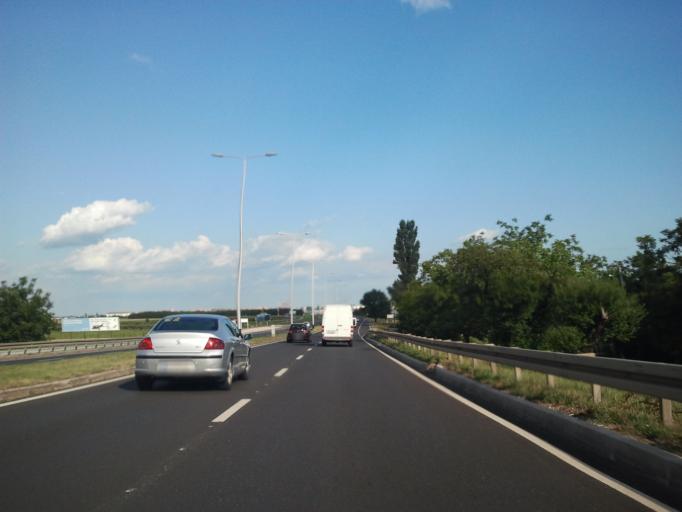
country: HR
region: Zagrebacka
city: Gradici
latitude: 45.7275
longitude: 16.0343
